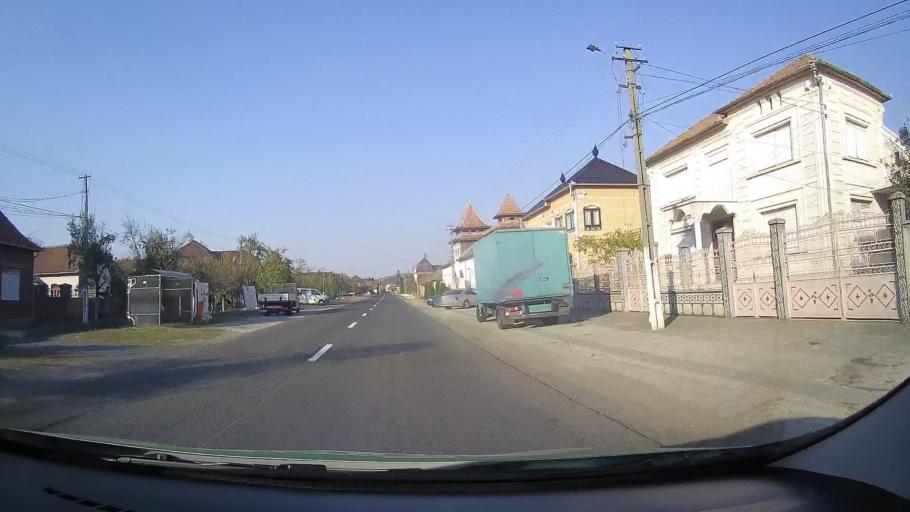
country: RO
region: Arad
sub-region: Comuna Covasint
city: Covasint
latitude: 46.1961
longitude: 21.6071
